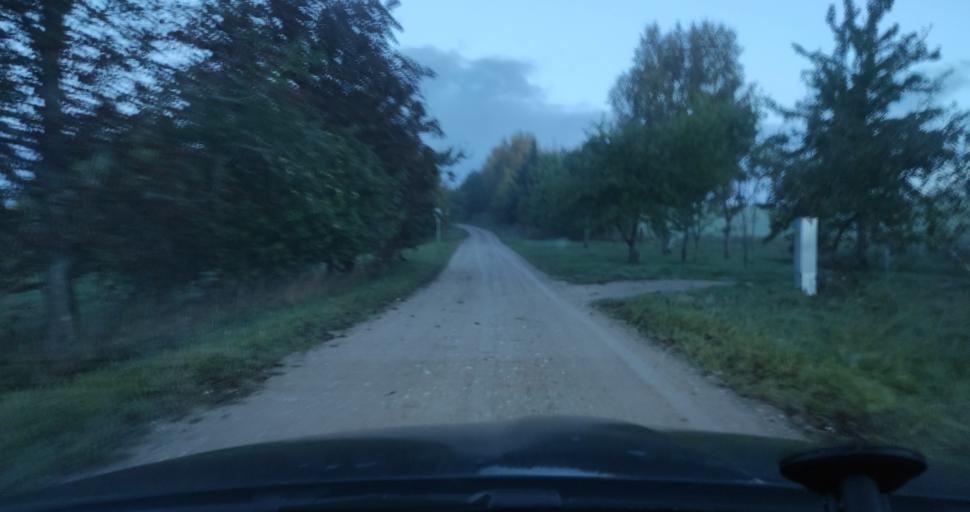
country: LV
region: Kuldigas Rajons
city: Kuldiga
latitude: 56.8852
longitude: 21.8173
